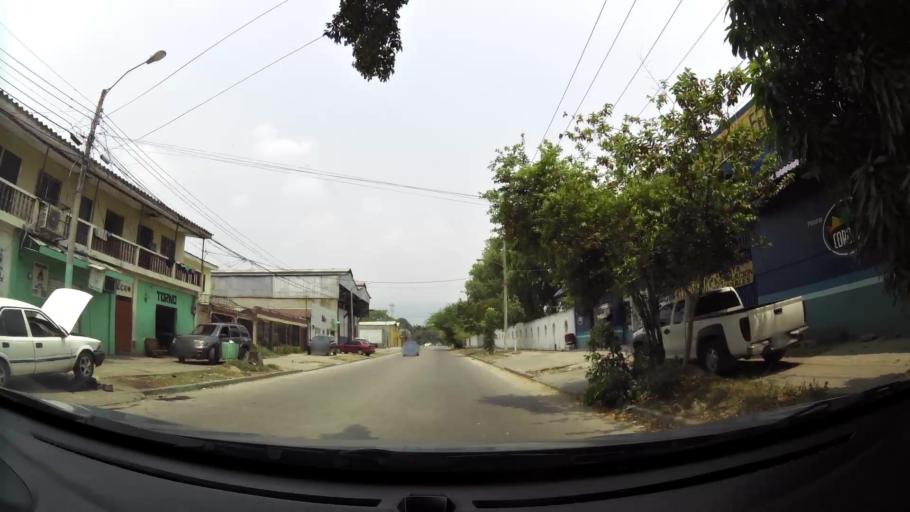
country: HN
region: Cortes
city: San Pedro Sula
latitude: 15.4855
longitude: -88.0124
